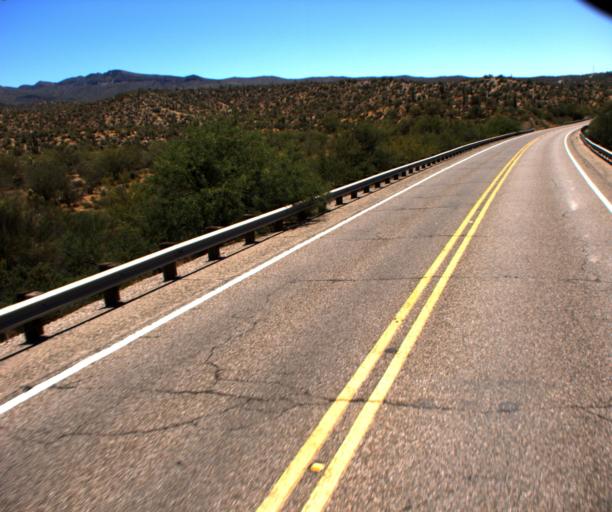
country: US
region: Arizona
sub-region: Pinal County
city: Kearny
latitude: 33.1153
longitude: -110.9592
